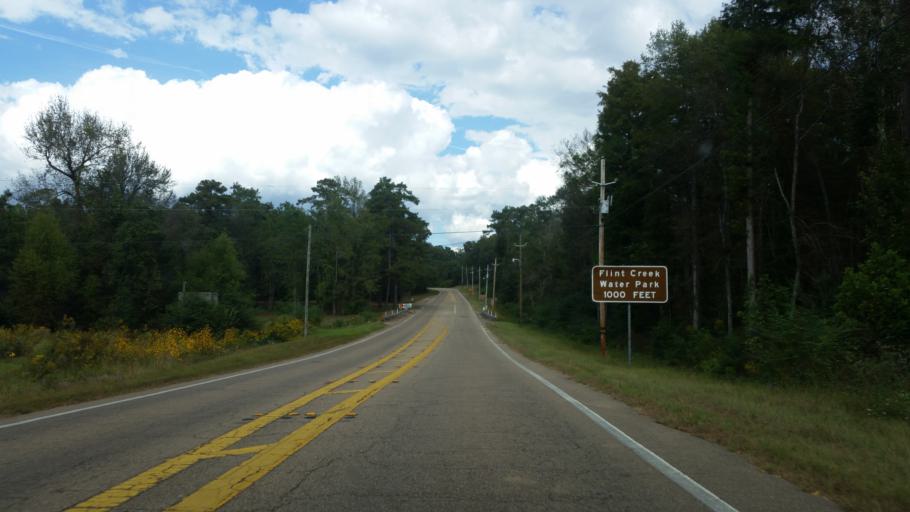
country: US
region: Mississippi
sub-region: Stone County
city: Wiggins
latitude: 30.8694
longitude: -89.1219
